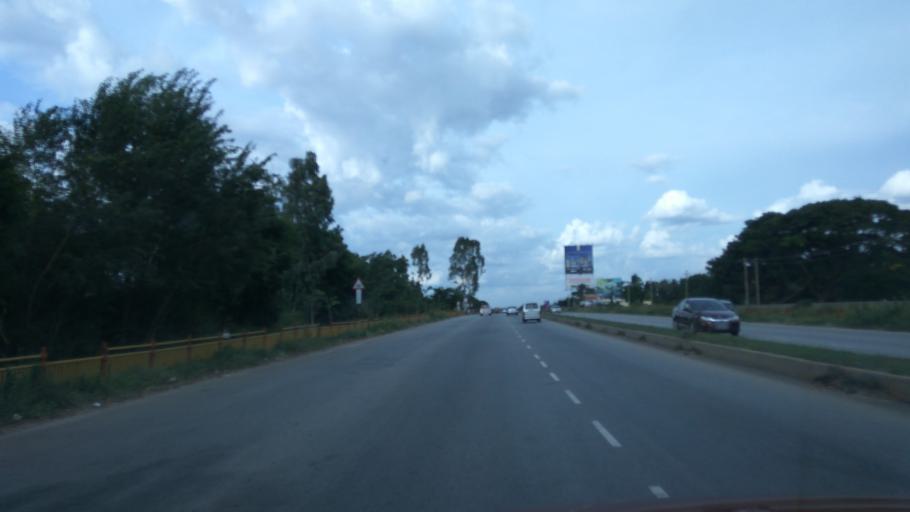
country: IN
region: Karnataka
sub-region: Bangalore Rural
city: Devanhalli
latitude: 13.2247
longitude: 77.6854
